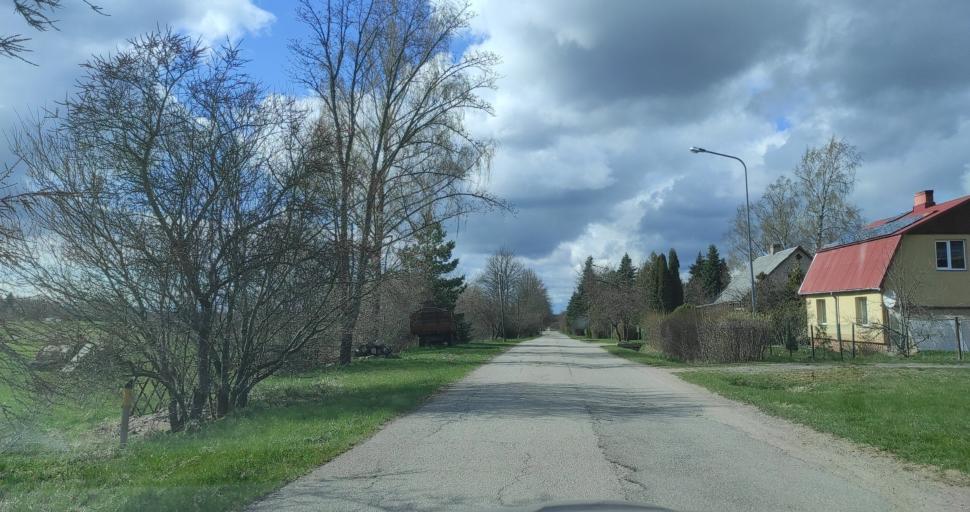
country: LV
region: Aizpute
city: Aizpute
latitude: 56.7134
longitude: 21.5930
